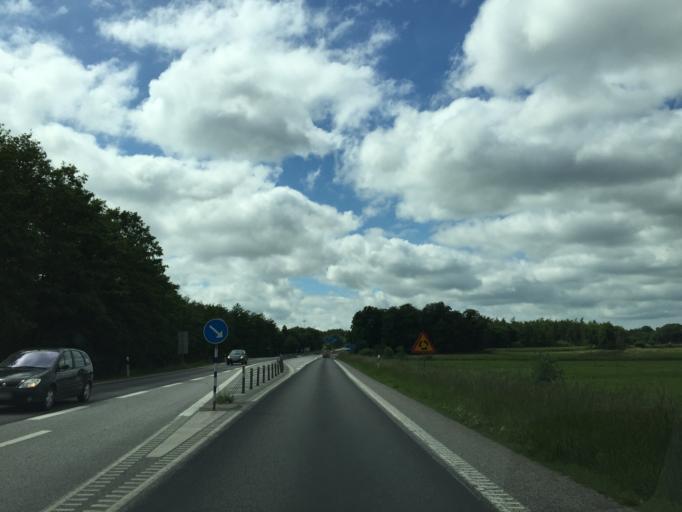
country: SE
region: Skane
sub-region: Trelleborgs Kommun
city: Anderslov
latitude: 55.5078
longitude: 13.3314
